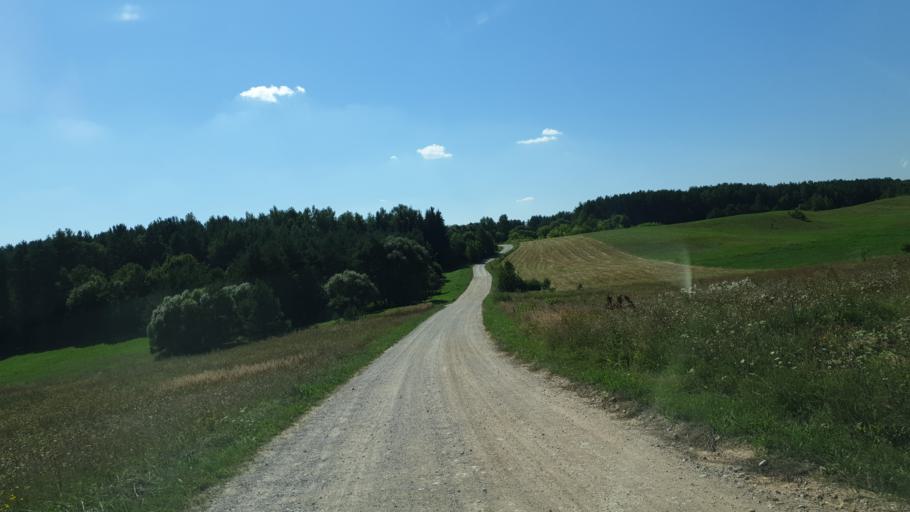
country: LT
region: Vilnius County
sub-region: Vilniaus Rajonas
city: Vievis
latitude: 54.8928
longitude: 24.8631
